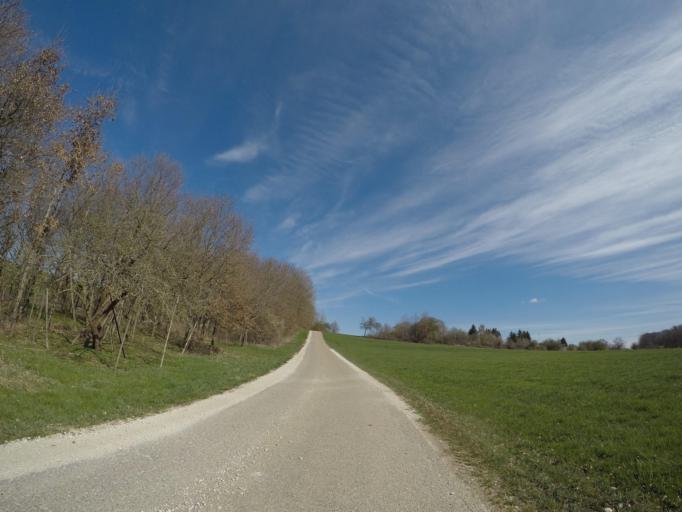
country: DE
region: Baden-Wuerttemberg
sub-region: Tuebingen Region
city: Mehrstetten
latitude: 48.3344
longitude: 9.5554
